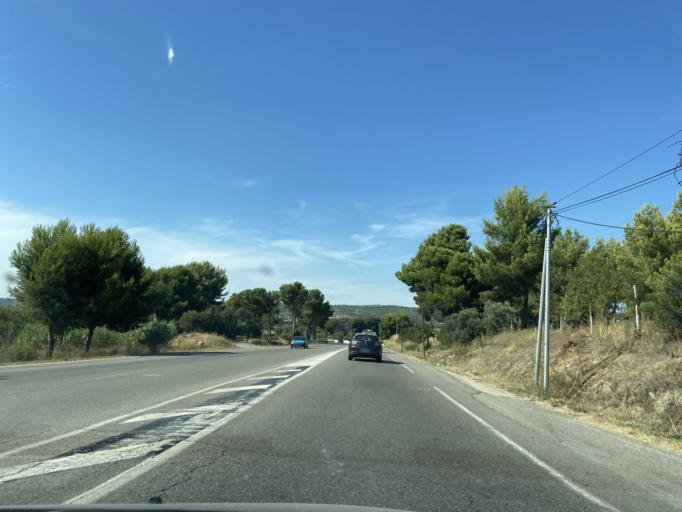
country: FR
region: Provence-Alpes-Cote d'Azur
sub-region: Departement des Bouches-du-Rhone
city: La Fare-les-Oliviers
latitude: 43.5273
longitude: 5.1965
